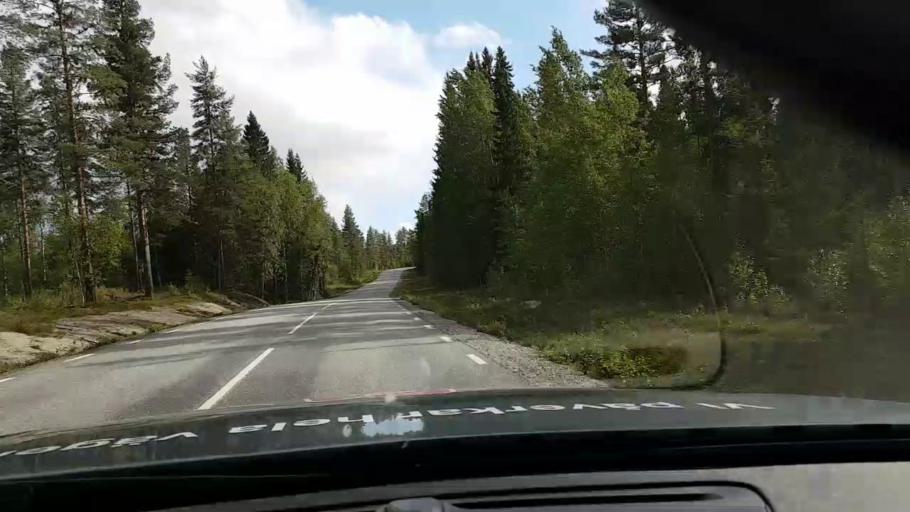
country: SE
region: Vaesternorrland
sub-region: OErnskoeldsviks Kommun
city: Bredbyn
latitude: 63.6471
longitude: 17.8946
